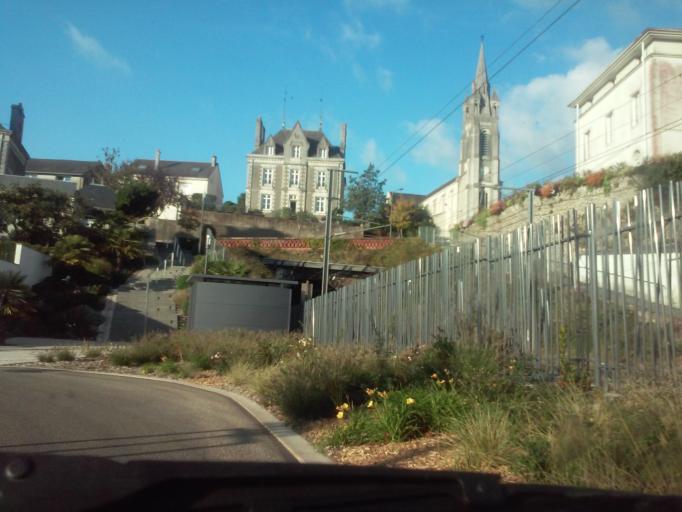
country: FR
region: Pays de la Loire
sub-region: Departement de la Loire-Atlantique
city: Pontchateau
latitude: 47.4369
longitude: -2.0885
